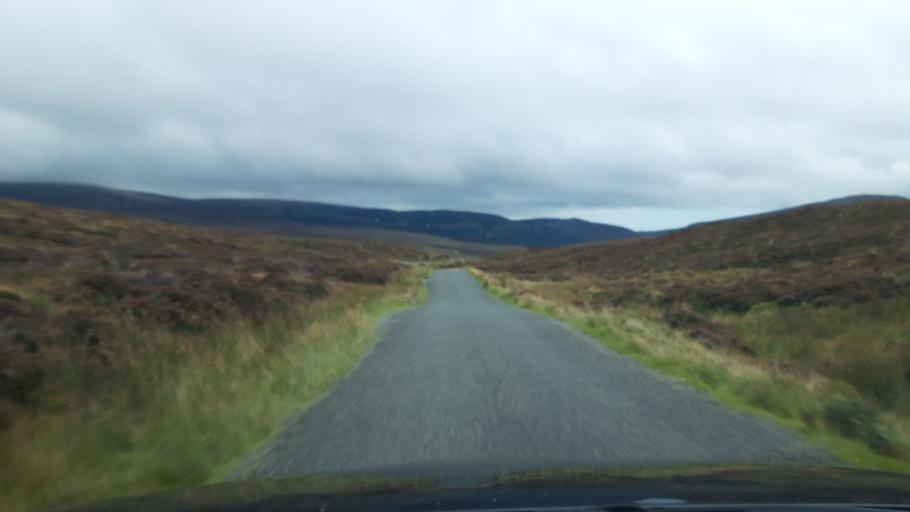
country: IE
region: Leinster
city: Ballyboden
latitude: 53.1345
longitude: -6.3050
